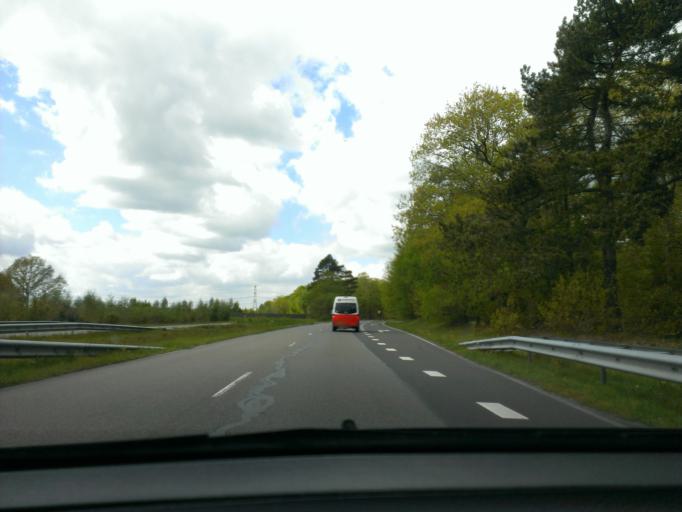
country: NL
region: Drenthe
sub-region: Gemeente Emmen
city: Emmen
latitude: 52.7599
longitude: 6.8571
